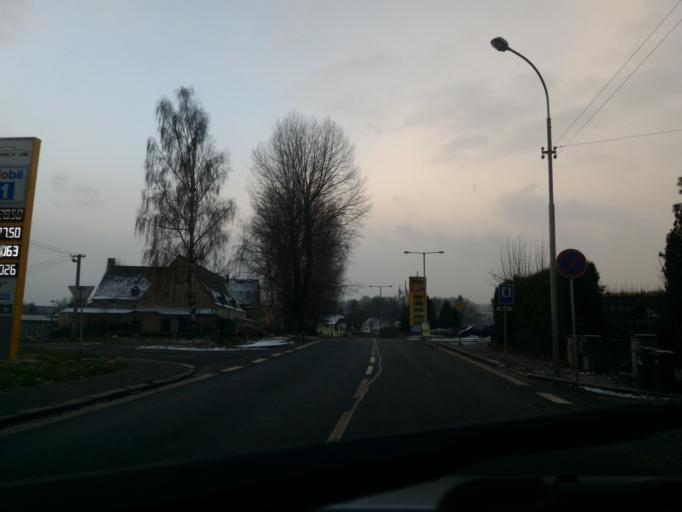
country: CZ
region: Ustecky
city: Varnsdorf
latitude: 50.9187
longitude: 14.6072
